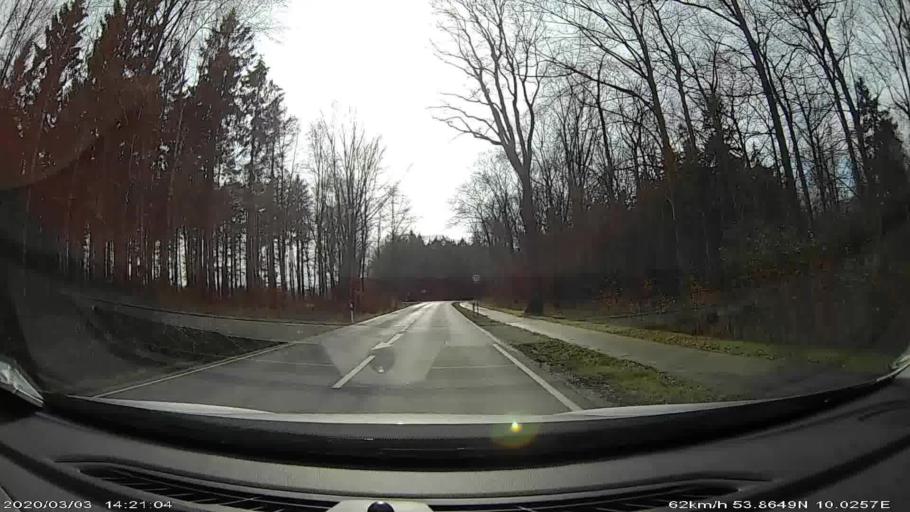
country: DE
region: Schleswig-Holstein
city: Kattendorf
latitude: 53.8647
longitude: 10.0255
